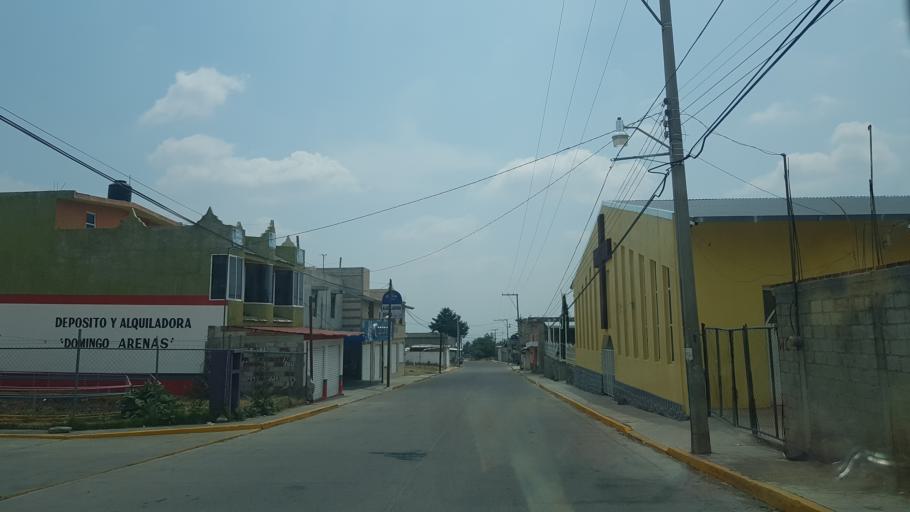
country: MX
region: Puebla
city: Domingo Arenas
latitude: 19.1393
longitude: -98.4490
